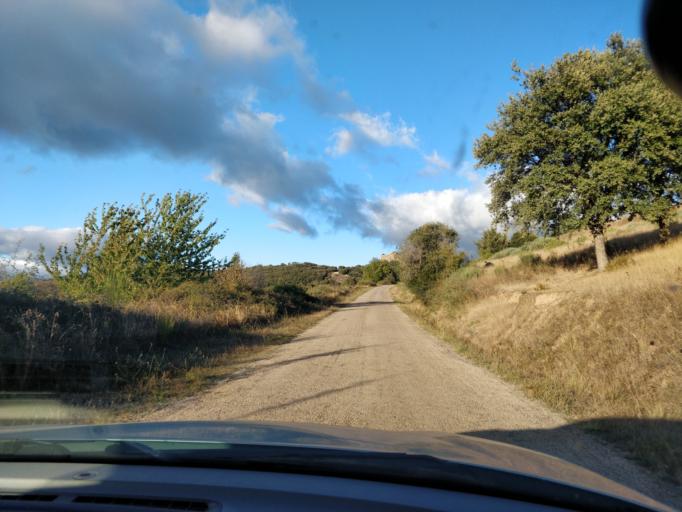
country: ES
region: Castille and Leon
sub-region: Provincia de Leon
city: Borrenes
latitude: 42.4854
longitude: -6.6995
